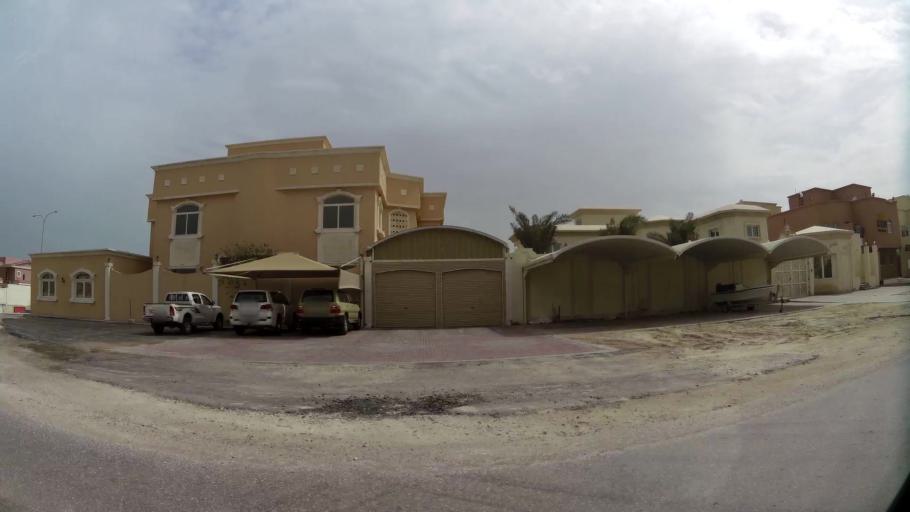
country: QA
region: Baladiyat ar Rayyan
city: Ar Rayyan
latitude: 25.3511
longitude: 51.4652
